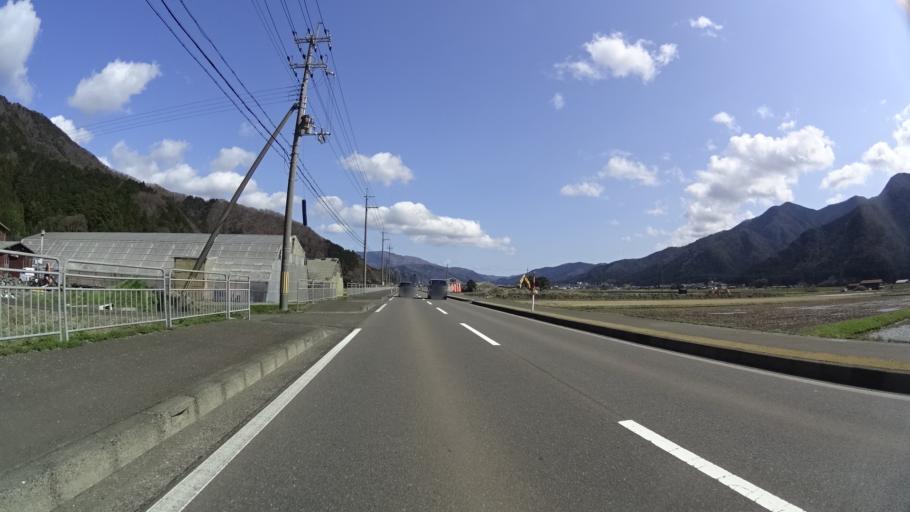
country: JP
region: Fukui
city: Obama
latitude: 35.4734
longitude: 135.8351
